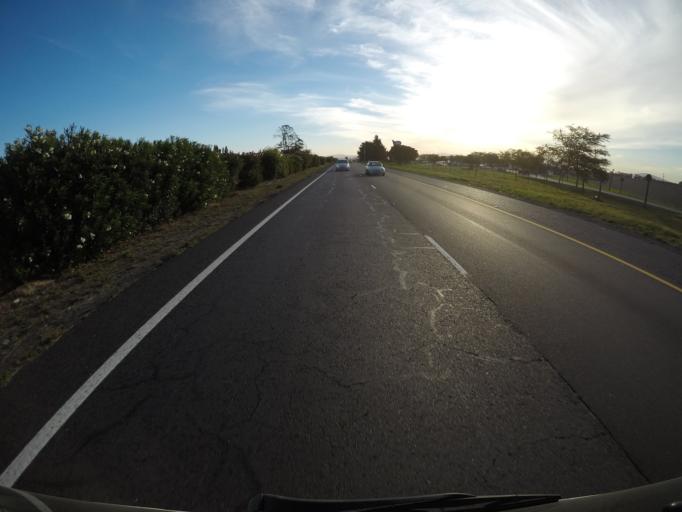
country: ZA
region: Western Cape
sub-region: City of Cape Town
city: Kraaifontein
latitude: -33.8271
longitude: 18.7654
